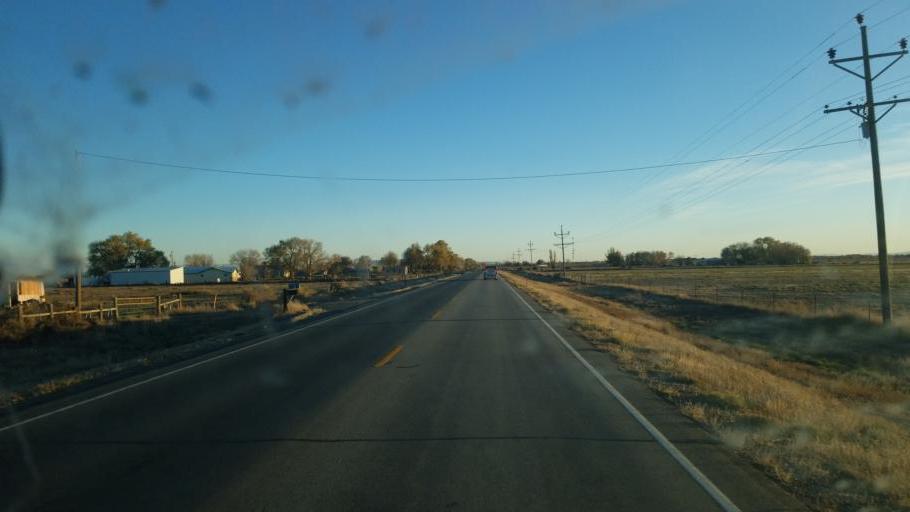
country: US
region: Colorado
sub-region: Alamosa County
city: Alamosa East
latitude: 37.5114
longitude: -105.8585
